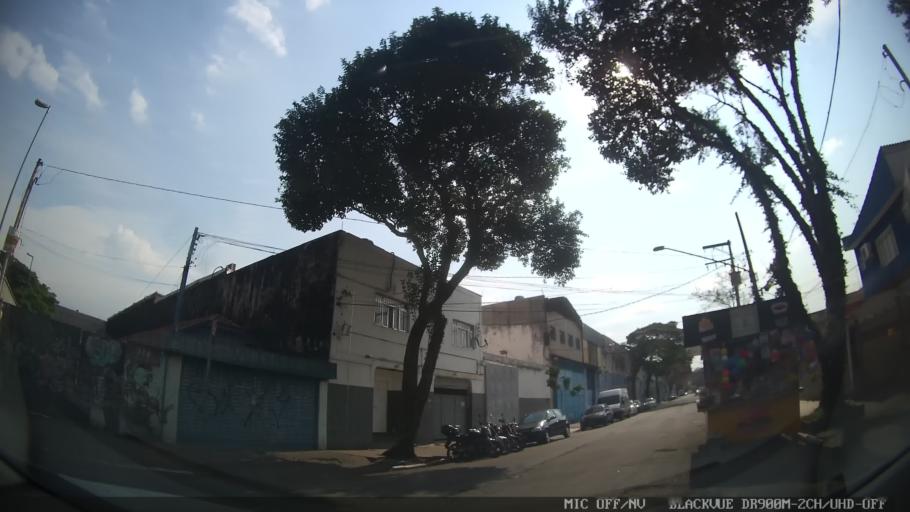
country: BR
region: Sao Paulo
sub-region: Sao Caetano Do Sul
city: Sao Caetano do Sul
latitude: -23.5959
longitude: -46.5930
